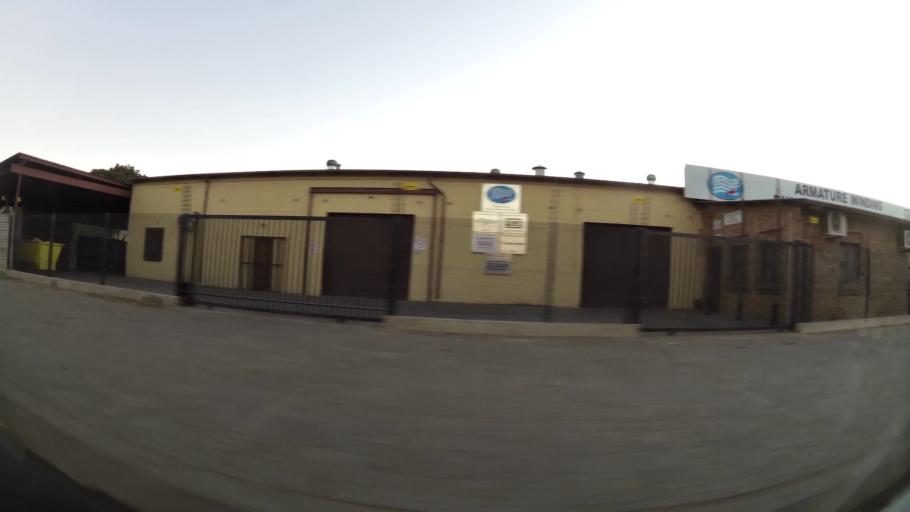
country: ZA
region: Northern Cape
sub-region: Frances Baard District Municipality
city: Kimberley
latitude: -28.7159
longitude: 24.7720
